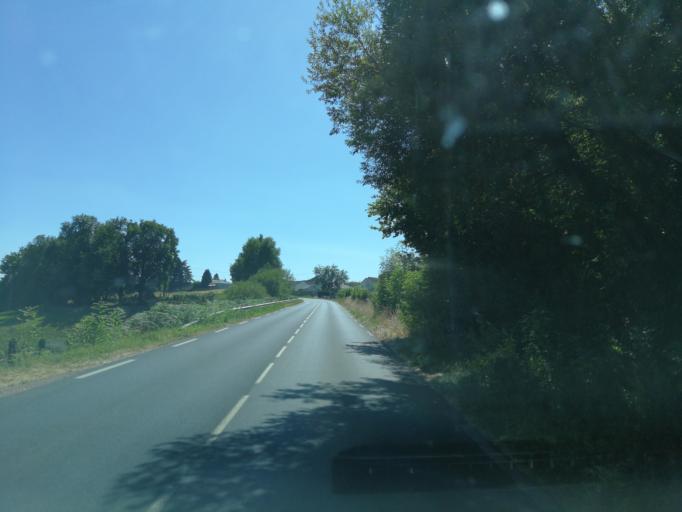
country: FR
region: Limousin
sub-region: Departement de la Correze
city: Sainte-Fereole
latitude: 45.2271
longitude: 1.5867
